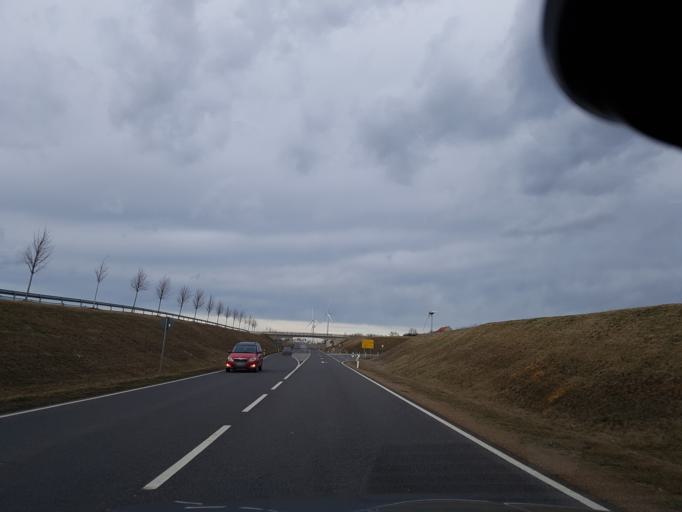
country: DE
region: Saxony
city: Niederstriegis
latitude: 51.0511
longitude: 13.1172
